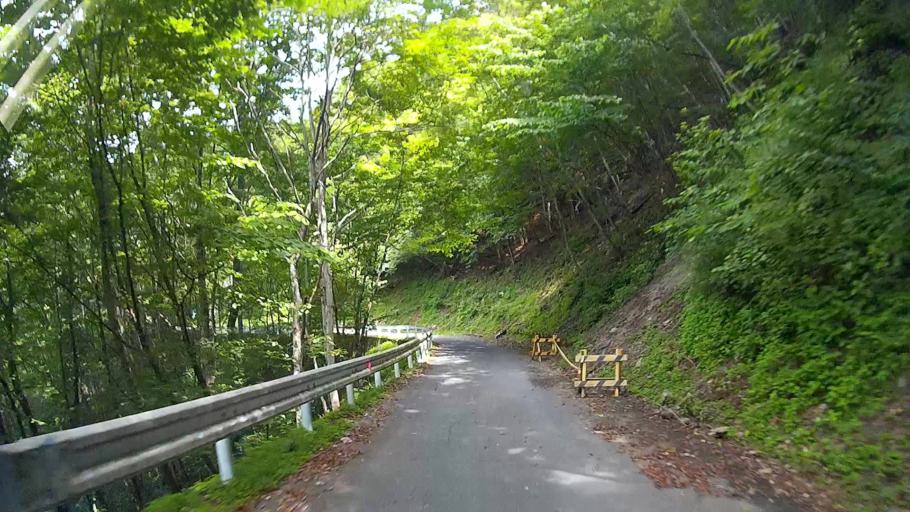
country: JP
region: Saitama
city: Chichibu
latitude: 35.8849
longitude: 139.1128
